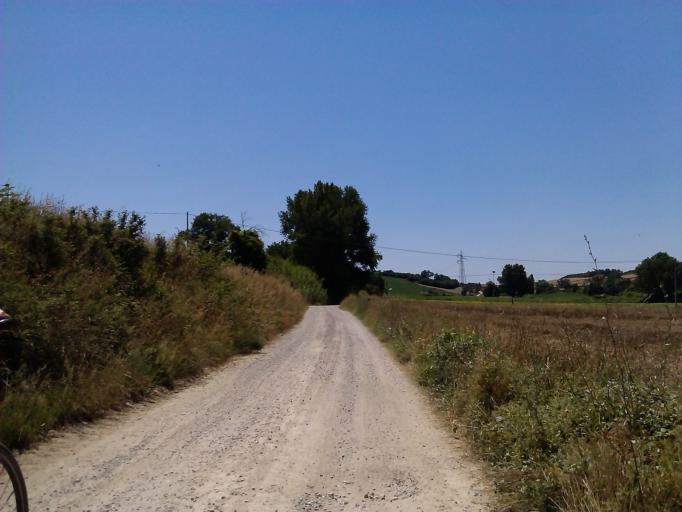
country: IT
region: Umbria
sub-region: Provincia di Terni
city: Fabro Scalo
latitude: 42.8470
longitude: 12.0417
